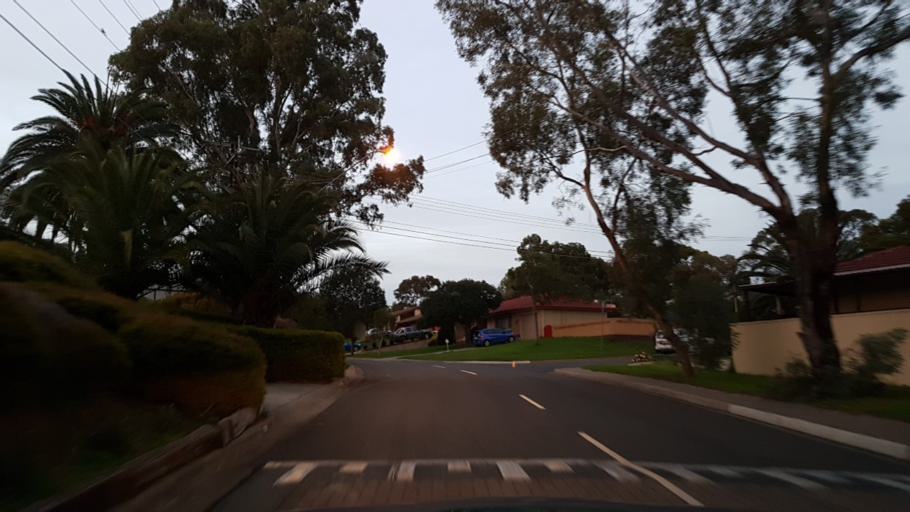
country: AU
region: South Australia
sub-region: Port Adelaide Enfield
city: Gilles Plains
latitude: -34.8396
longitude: 138.6596
